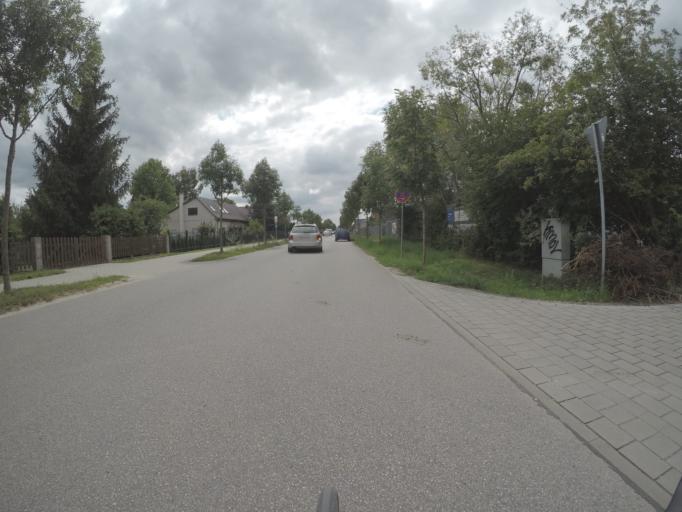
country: DE
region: Brandenburg
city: Brieselang
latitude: 52.5991
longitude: 12.9893
